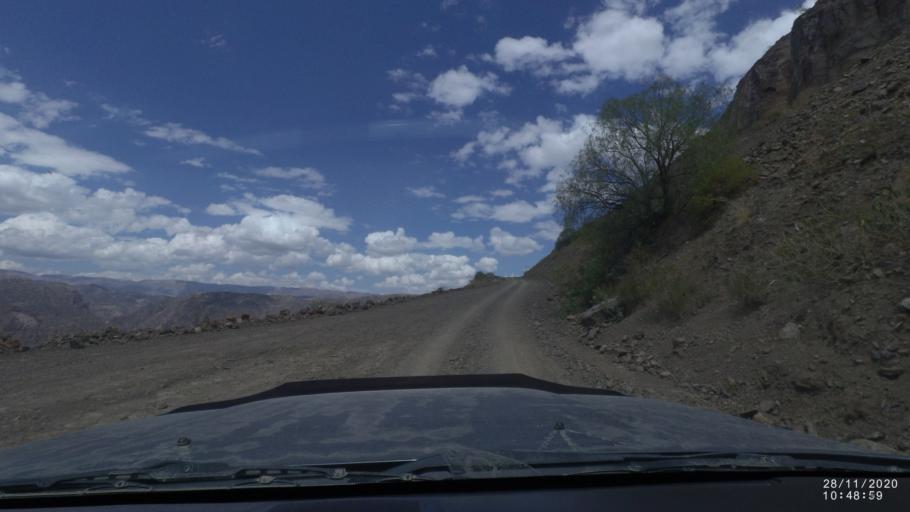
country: BO
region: Cochabamba
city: Capinota
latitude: -17.7862
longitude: -66.1206
